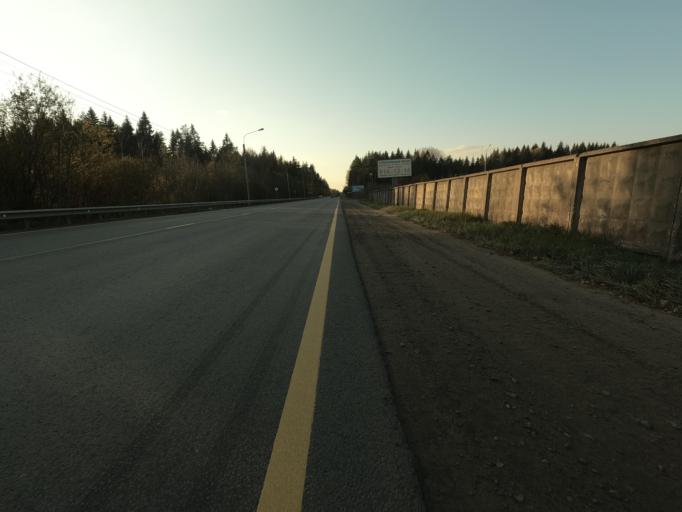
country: RU
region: St.-Petersburg
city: Pesochnyy
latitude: 60.1785
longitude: 30.1467
